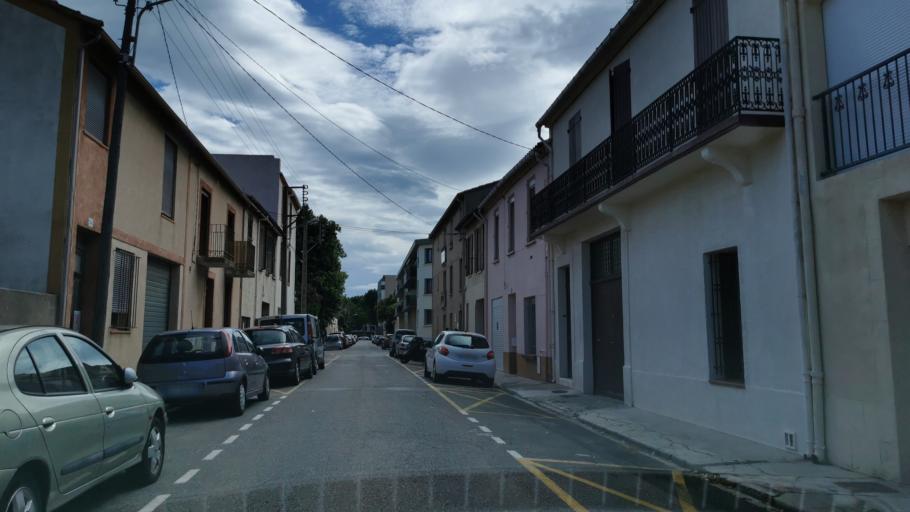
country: FR
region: Languedoc-Roussillon
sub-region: Departement de l'Aude
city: Narbonne
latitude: 43.1826
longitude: 3.0126
